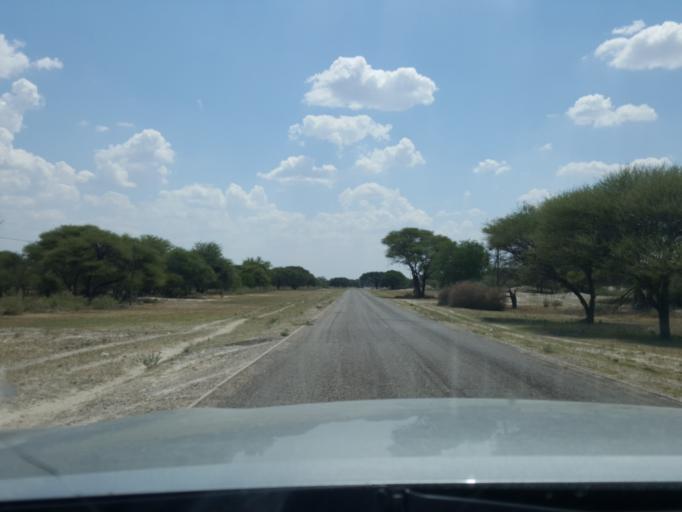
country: BW
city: Tsau
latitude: -20.1803
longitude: 22.4644
